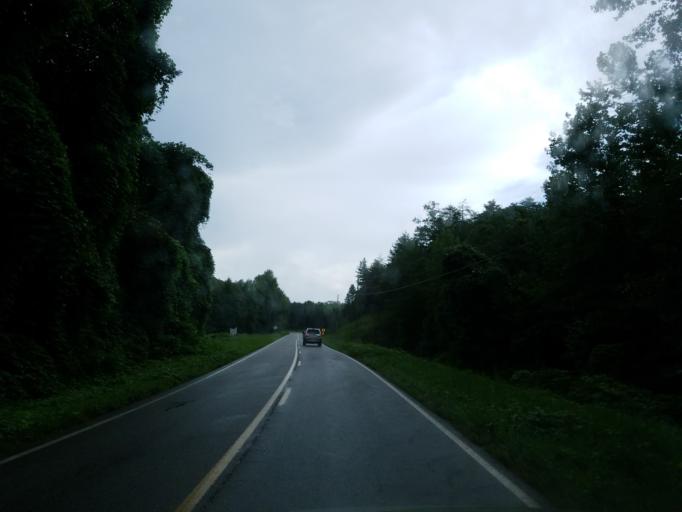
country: US
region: Georgia
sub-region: Lumpkin County
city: Dahlonega
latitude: 34.5485
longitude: -83.8841
